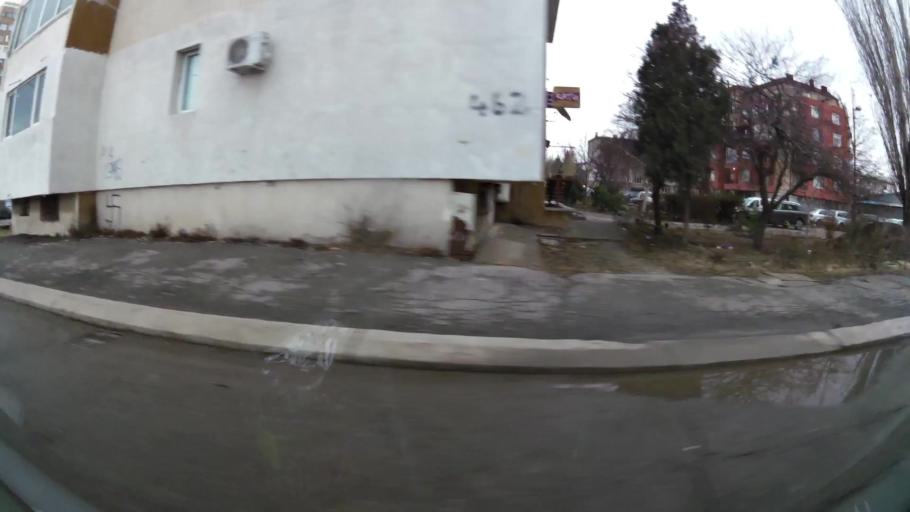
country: BG
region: Sofia-Capital
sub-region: Stolichna Obshtina
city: Sofia
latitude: 42.7343
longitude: 23.2974
